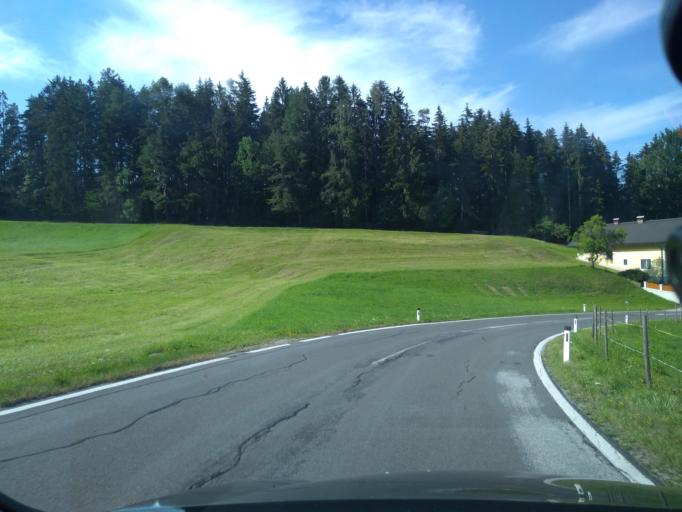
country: AT
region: Styria
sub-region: Politischer Bezirk Graz-Umgebung
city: Semriach
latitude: 47.2673
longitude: 15.4275
